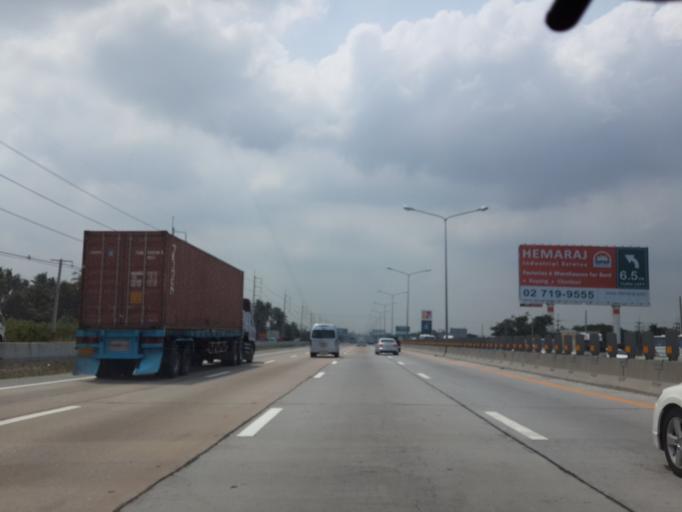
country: TH
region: Chon Buri
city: Si Racha
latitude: 13.1976
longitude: 101.0009
